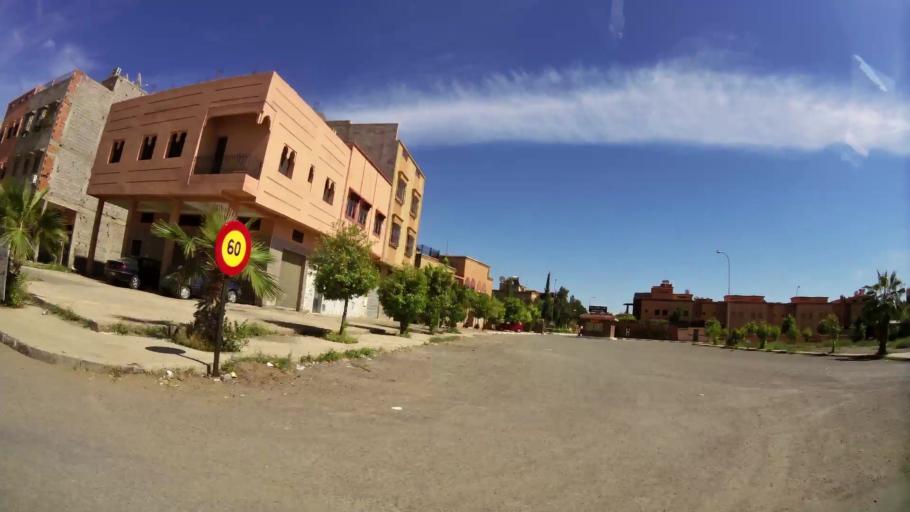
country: MA
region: Marrakech-Tensift-Al Haouz
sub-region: Marrakech
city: Marrakesh
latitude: 31.6400
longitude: -8.1068
